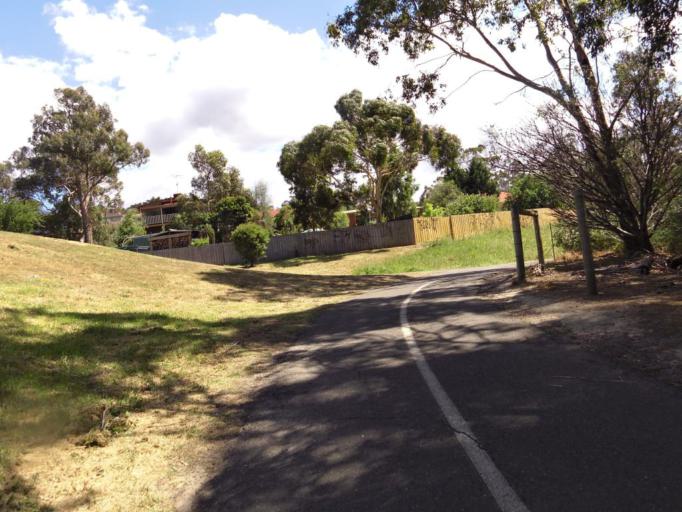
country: AU
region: Victoria
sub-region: Nillumbik
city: Eltham North
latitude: -37.6943
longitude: 145.1510
